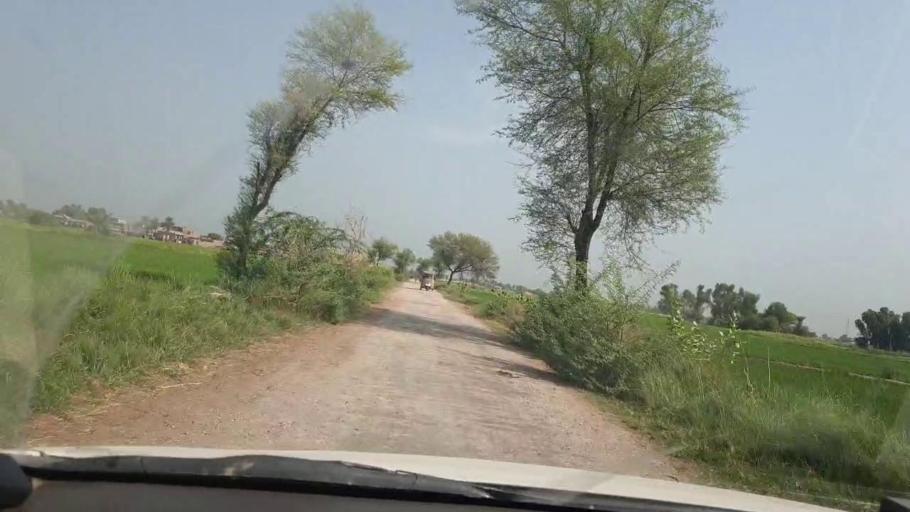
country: PK
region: Sindh
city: Chak
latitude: 27.8343
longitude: 68.7990
